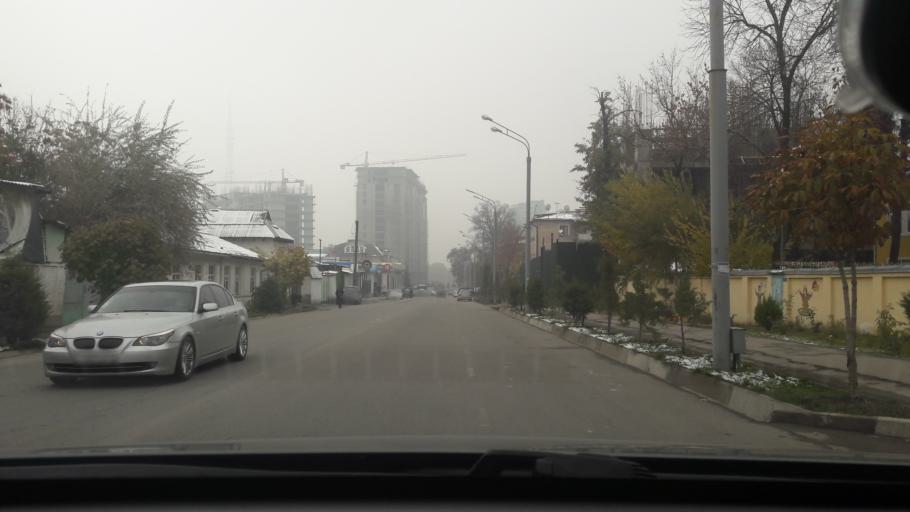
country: TJ
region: Dushanbe
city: Dushanbe
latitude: 38.5782
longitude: 68.8002
